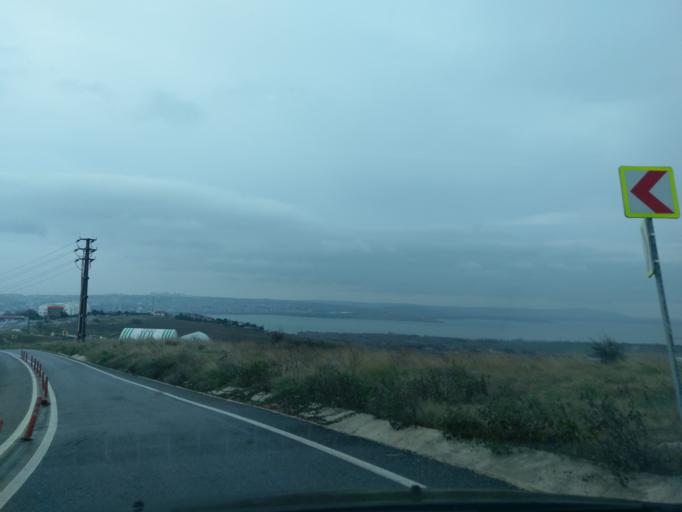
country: TR
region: Istanbul
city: Bueyuekcekmece
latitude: 41.0273
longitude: 28.6099
